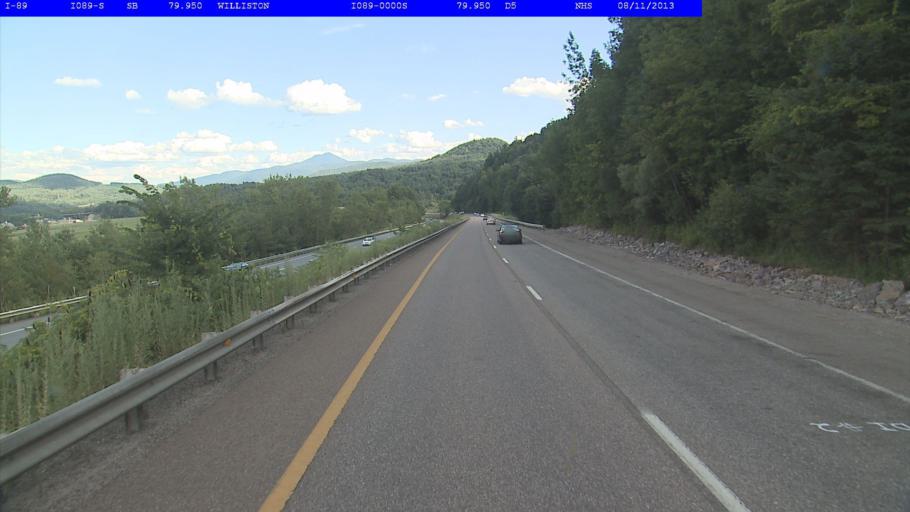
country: US
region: Vermont
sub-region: Chittenden County
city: Williston
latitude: 44.4292
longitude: -73.0367
